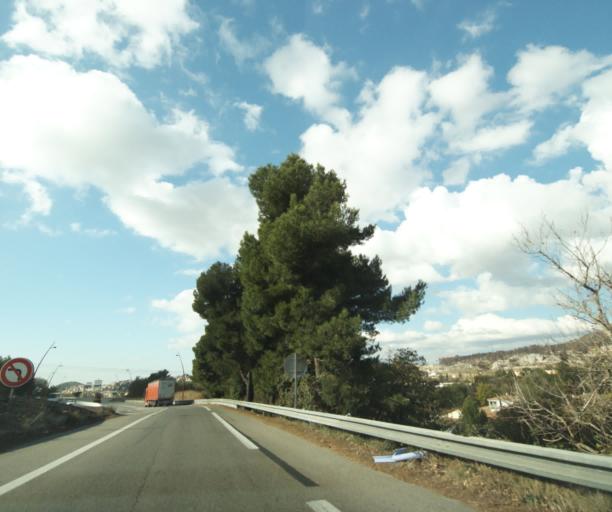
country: FR
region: Provence-Alpes-Cote d'Azur
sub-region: Departement des Bouches-du-Rhone
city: Les Pennes-Mirabeau
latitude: 43.4083
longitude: 5.3290
